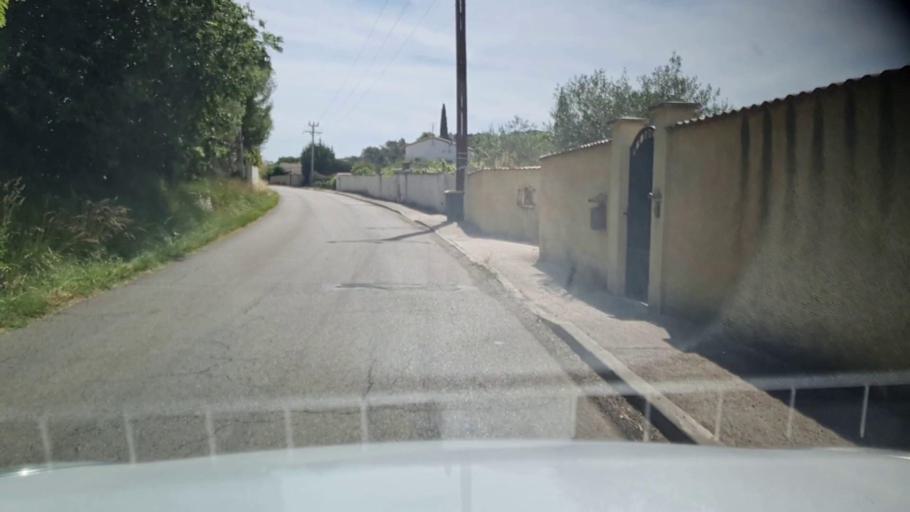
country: FR
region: Languedoc-Roussillon
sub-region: Departement du Gard
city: Nages-et-Solorgues
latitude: 43.7892
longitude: 4.2349
